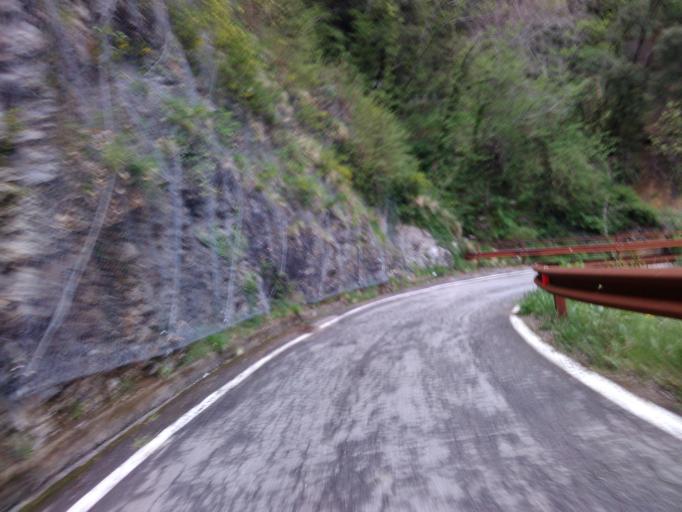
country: IT
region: Tuscany
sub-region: Provincia di Lucca
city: Pontestazzemese
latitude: 43.9758
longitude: 10.2749
